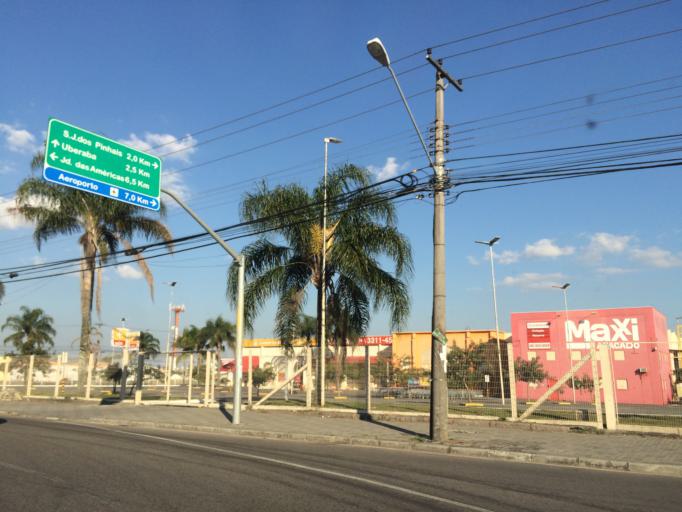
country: BR
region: Parana
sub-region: Sao Jose Dos Pinhais
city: Sao Jose dos Pinhais
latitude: -25.5181
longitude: -49.2306
